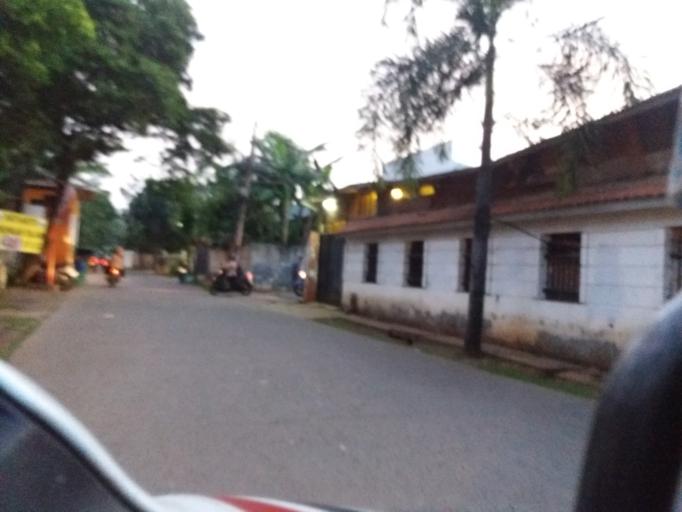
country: ID
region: Jakarta Raya
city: Jakarta
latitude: -6.2422
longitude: 106.8149
